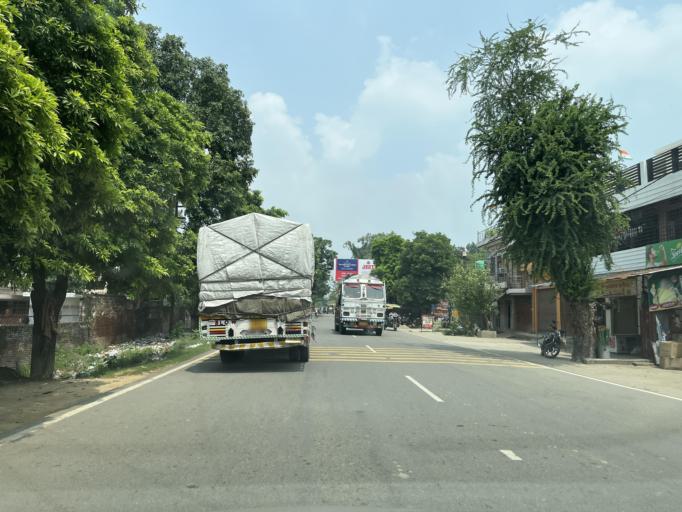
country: IN
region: Uttar Pradesh
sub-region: Bijnor
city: Najibabad
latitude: 29.5968
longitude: 78.3395
